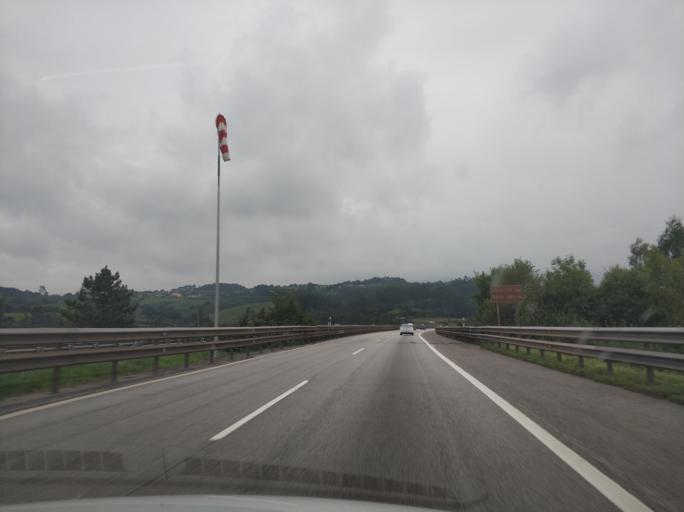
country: ES
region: Asturias
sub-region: Province of Asturias
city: Lugones
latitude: 43.4728
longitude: -5.7904
